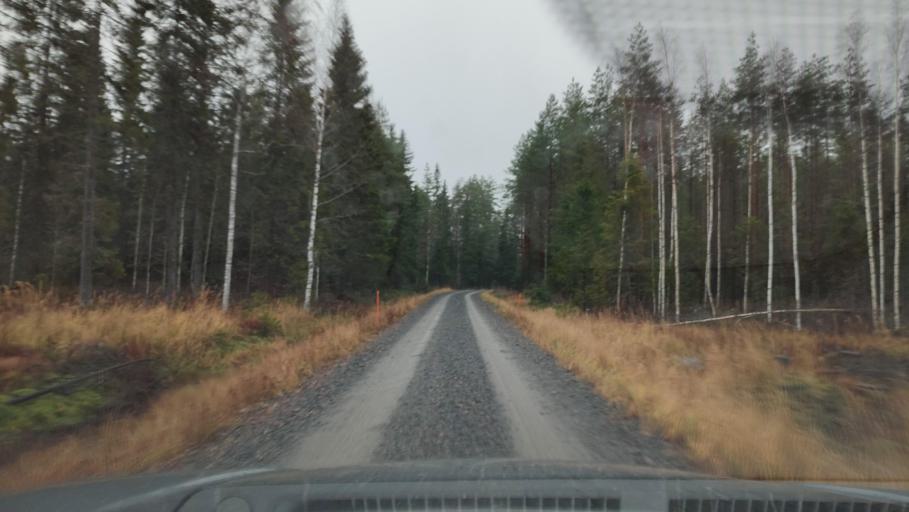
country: FI
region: Southern Ostrobothnia
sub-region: Suupohja
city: Karijoki
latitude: 62.1378
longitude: 21.6269
